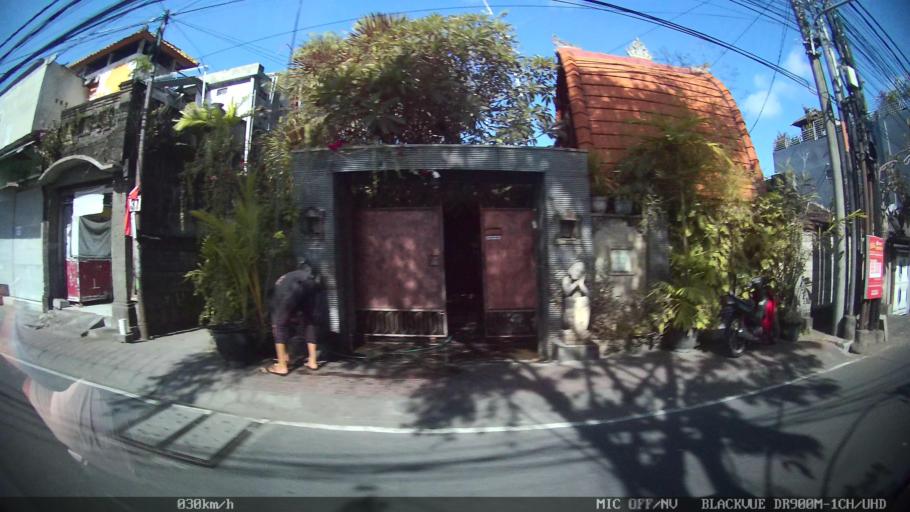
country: ID
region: Bali
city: Jabajero
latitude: -8.7343
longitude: 115.1704
